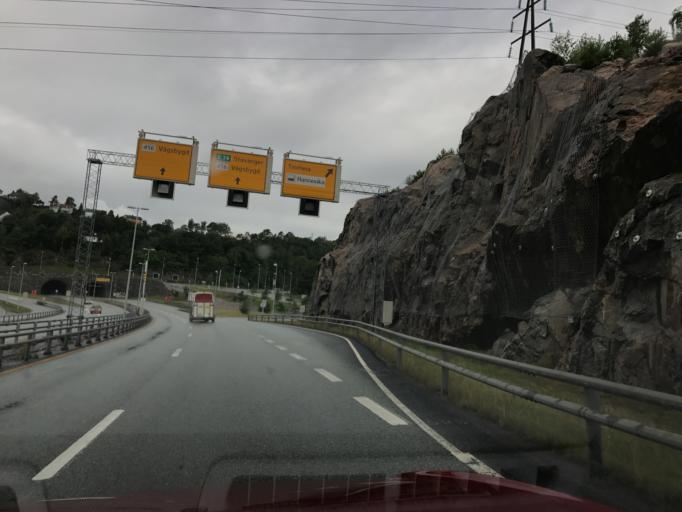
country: NO
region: Vest-Agder
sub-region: Kristiansand
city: Kristiansand
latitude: 58.1410
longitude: 7.9691
